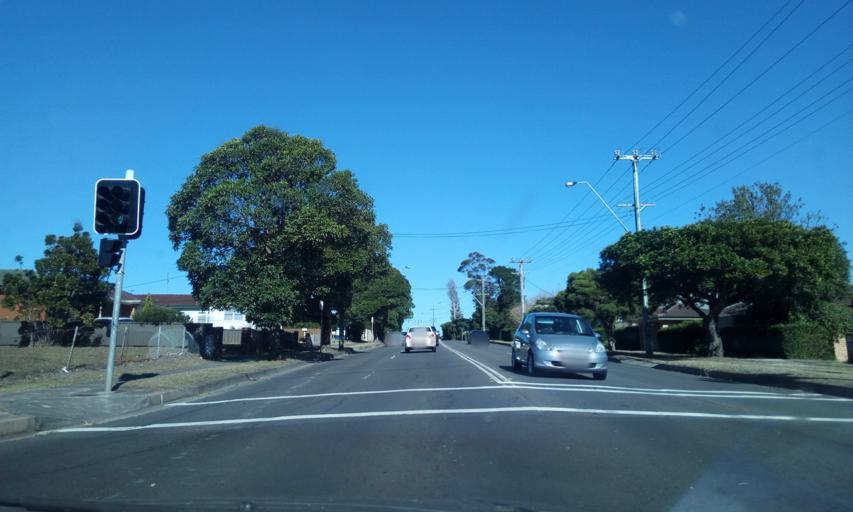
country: AU
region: New South Wales
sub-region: Wollongong
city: Dapto
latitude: -34.5031
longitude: 150.7885
